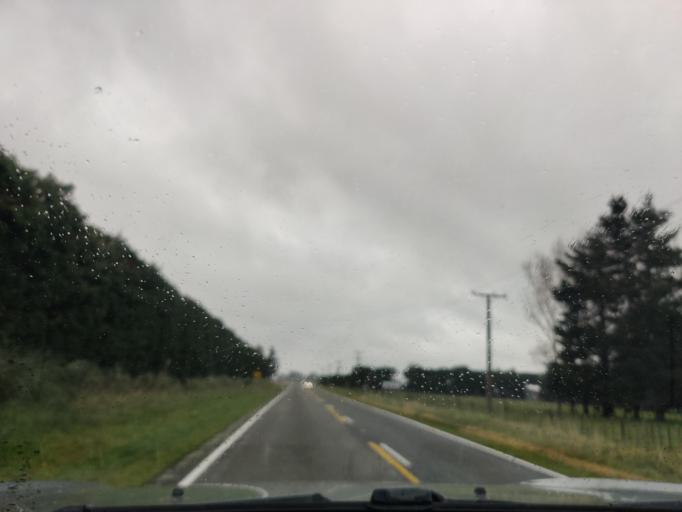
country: NZ
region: Hawke's Bay
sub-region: Hastings District
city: Hastings
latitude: -40.0169
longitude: 176.3534
